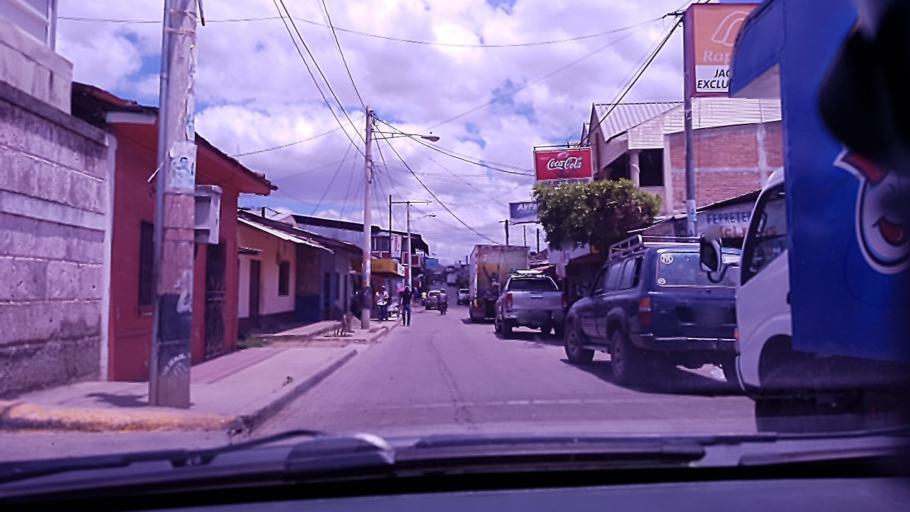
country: NI
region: Esteli
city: Condega
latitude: 13.3612
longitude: -86.3986
